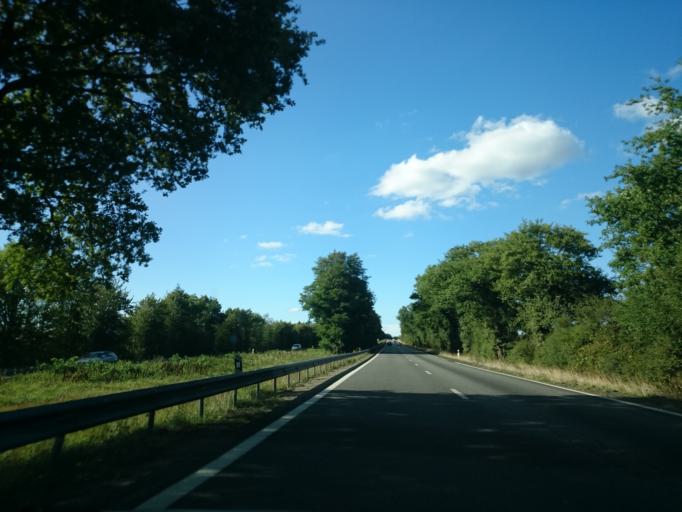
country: FR
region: Brittany
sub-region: Departement d'Ille-et-Vilaine
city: Grand-Fougeray
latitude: 47.7162
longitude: -1.7080
